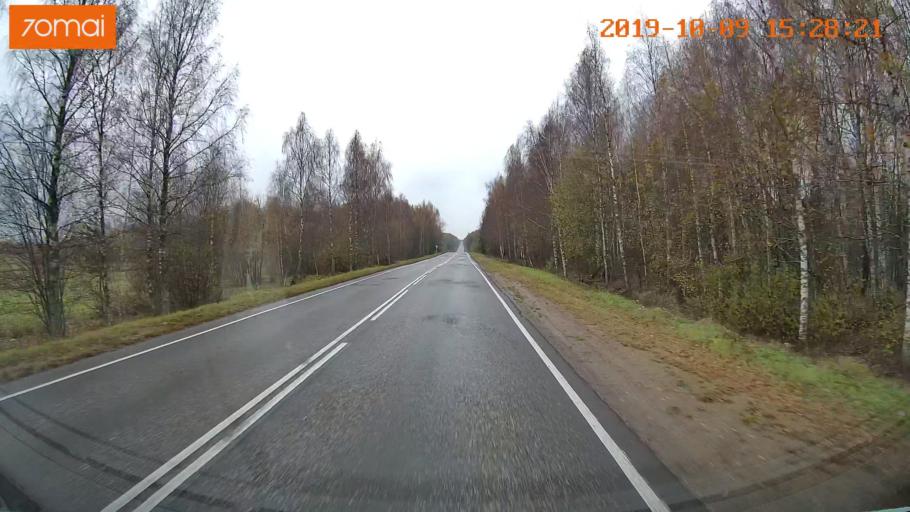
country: RU
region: Kostroma
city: Susanino
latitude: 58.0041
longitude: 41.3614
